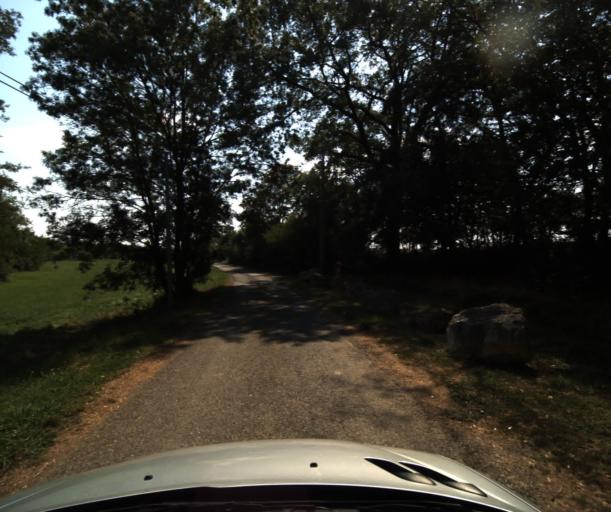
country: FR
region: Midi-Pyrenees
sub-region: Departement de la Haute-Garonne
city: Saint-Lys
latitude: 43.5122
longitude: 1.1701
